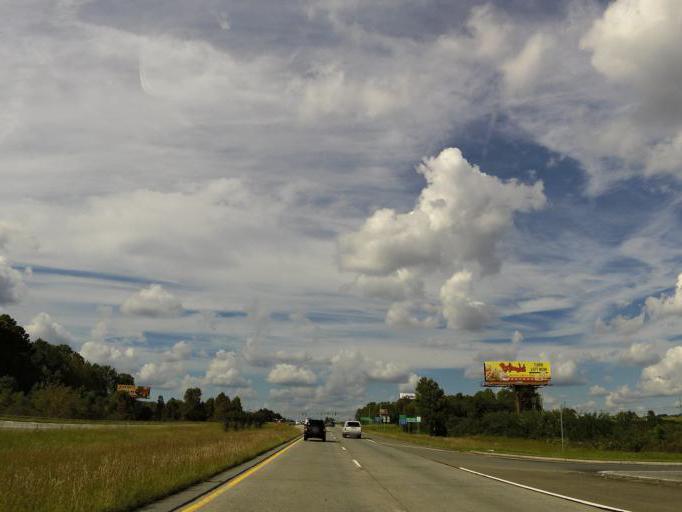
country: US
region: Georgia
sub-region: Pickens County
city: Jasper
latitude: 34.4629
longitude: -84.4571
